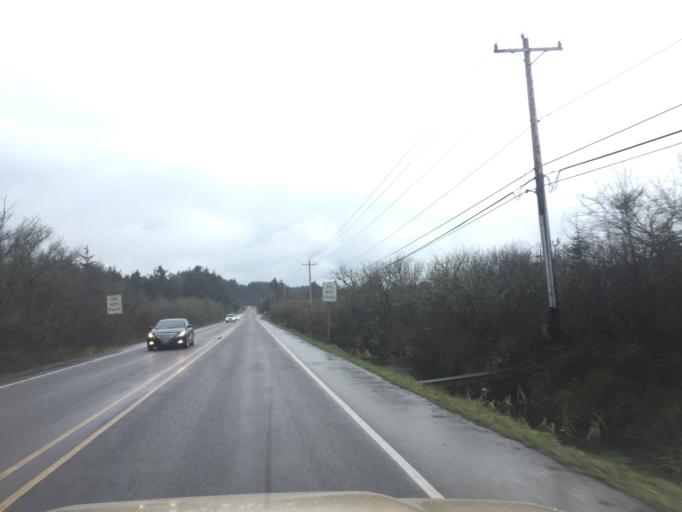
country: US
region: Oregon
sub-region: Lincoln County
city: Newport
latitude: 44.5977
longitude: -124.0599
